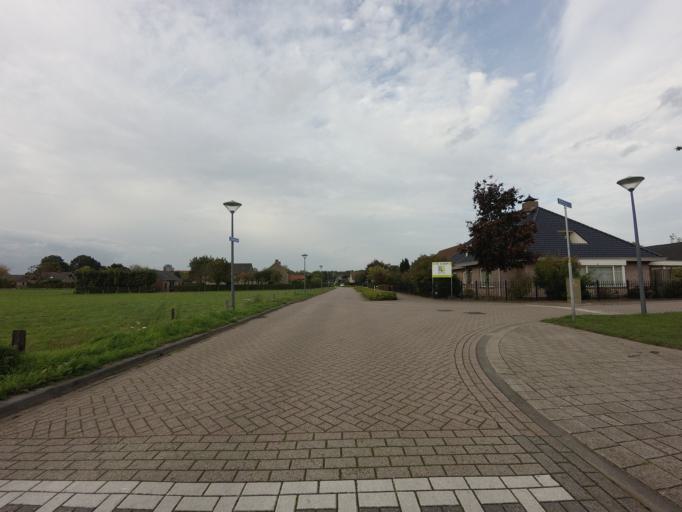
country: NL
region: North Brabant
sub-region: Gemeente Breda
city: Breda
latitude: 51.5982
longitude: 4.7327
